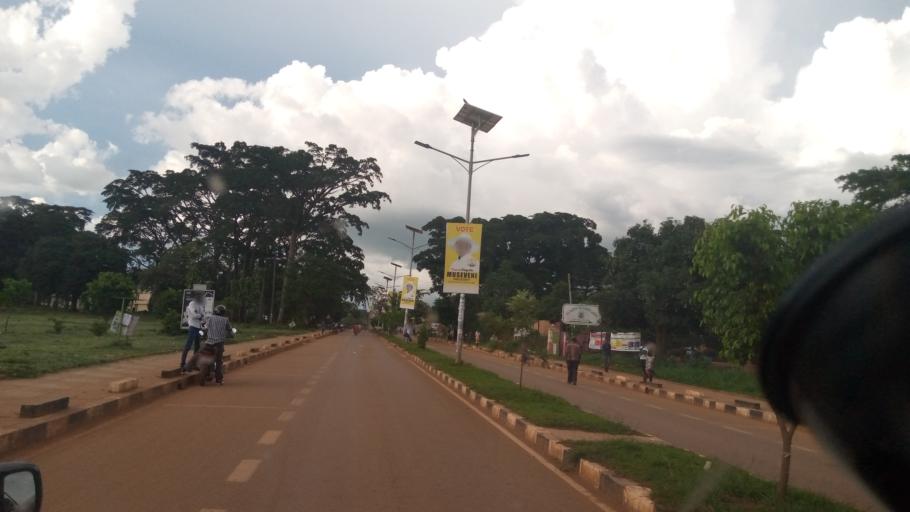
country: UG
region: Northern Region
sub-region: Lira District
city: Lira
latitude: 2.2463
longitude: 32.8992
